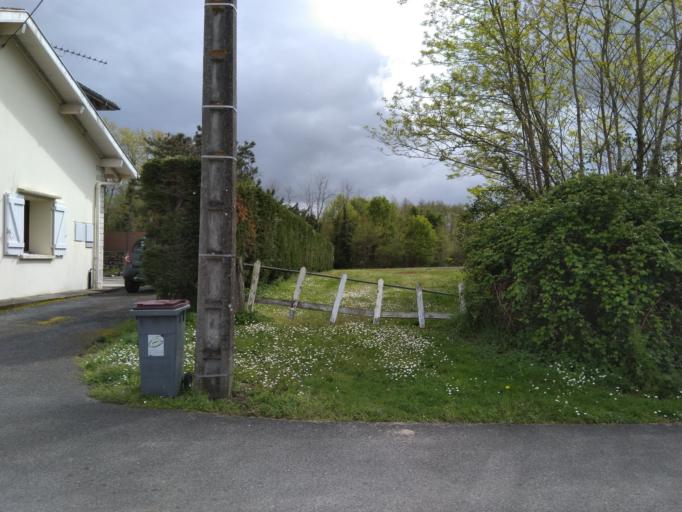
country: FR
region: Aquitaine
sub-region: Departement des Landes
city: Dax
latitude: 43.7106
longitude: -1.0349
